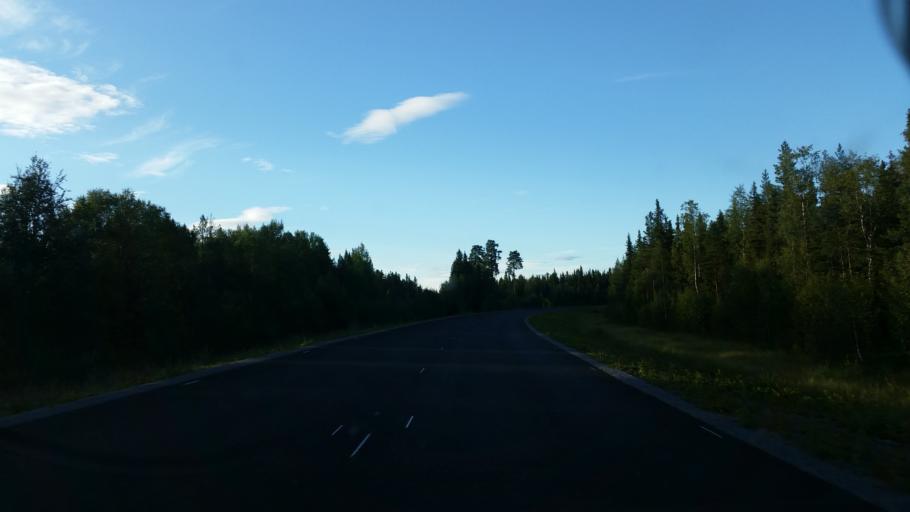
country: SE
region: Vaesterbotten
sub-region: Dorotea Kommun
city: Dorotea
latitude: 64.2810
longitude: 16.5038
